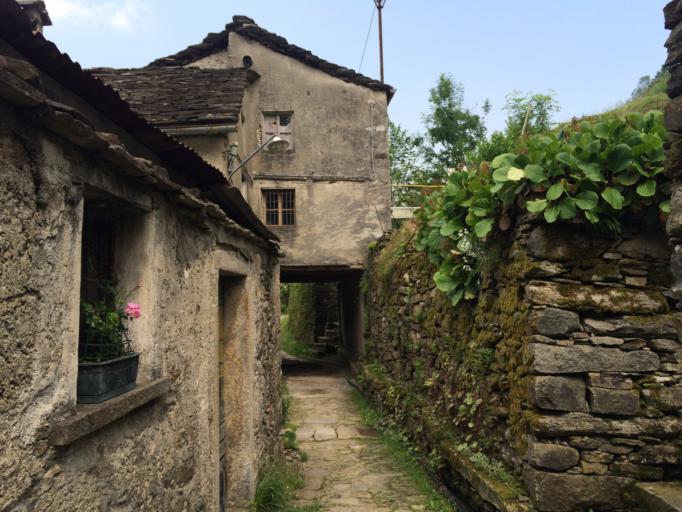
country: IT
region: Piedmont
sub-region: Provincia Verbano-Cusio-Ossola
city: Cavaglio-Spoccia
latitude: 46.0648
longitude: 8.6227
